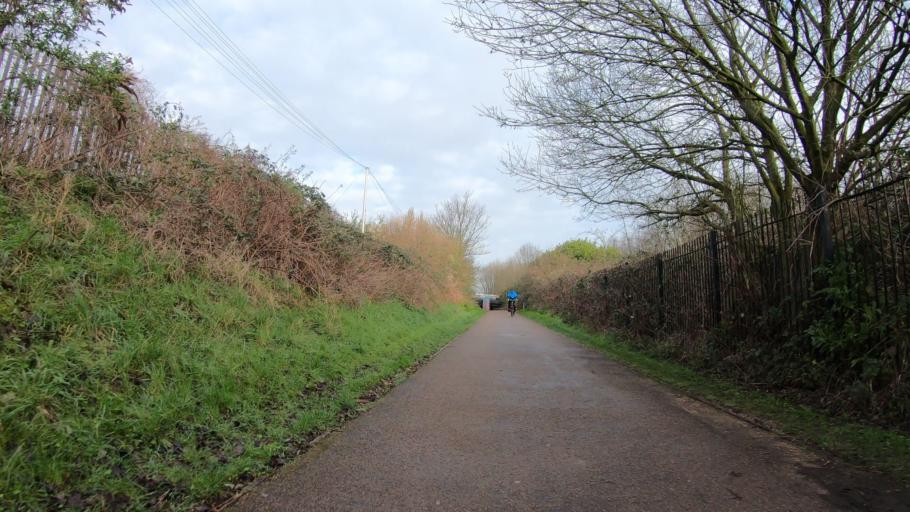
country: GB
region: England
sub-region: Greater London
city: Hackney
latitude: 51.5583
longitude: -0.0249
